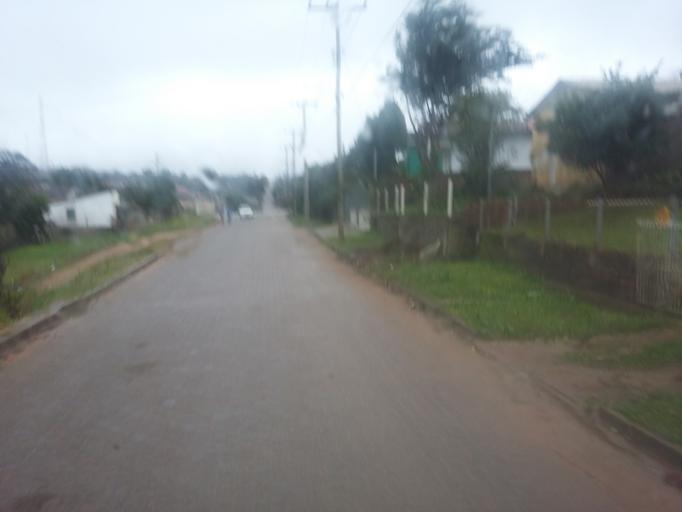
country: BR
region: Rio Grande do Sul
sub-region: Camaqua
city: Camaqua
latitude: -30.8392
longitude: -51.8125
